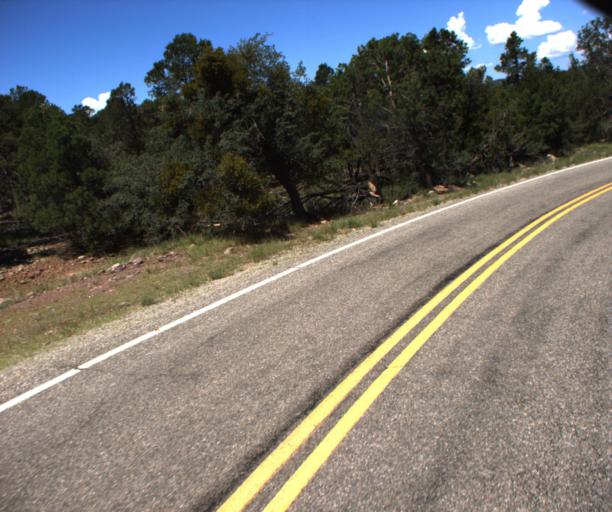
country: US
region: Arizona
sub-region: Greenlee County
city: Morenci
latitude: 33.3731
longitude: -109.3301
